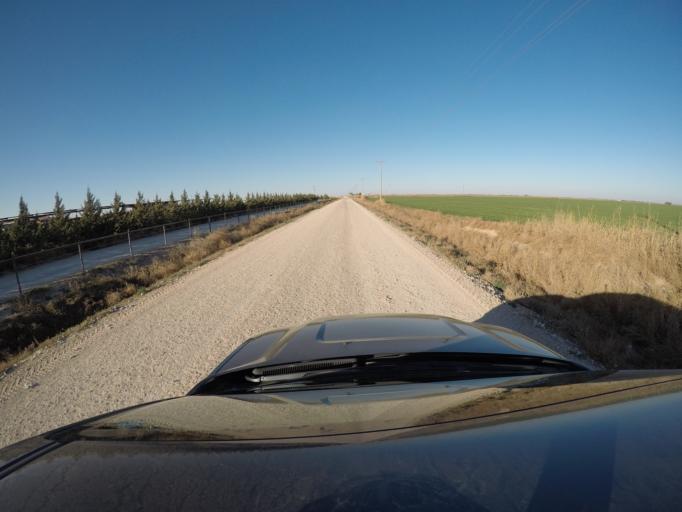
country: US
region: New Mexico
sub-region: Curry County
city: Texico
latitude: 34.3736
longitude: -103.1082
